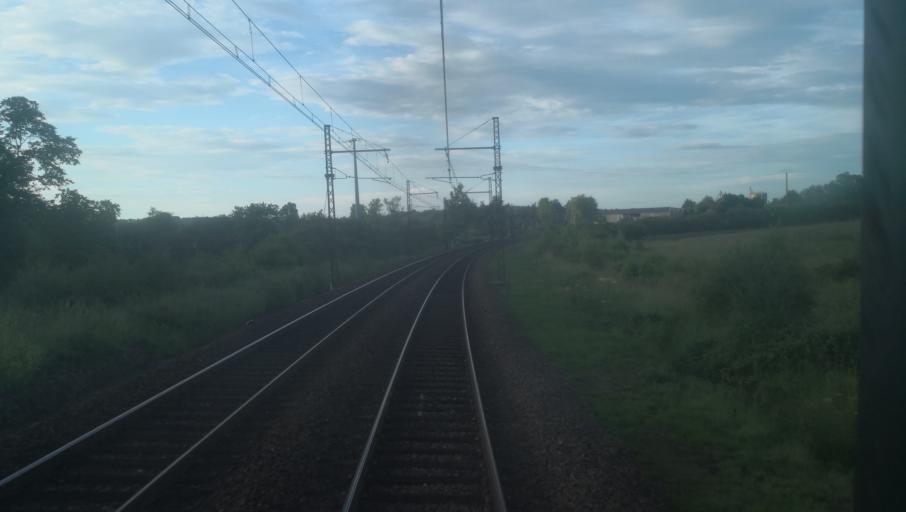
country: FR
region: Centre
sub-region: Departement de l'Indre
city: Argenton-sur-Creuse
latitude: 46.5133
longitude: 1.4992
